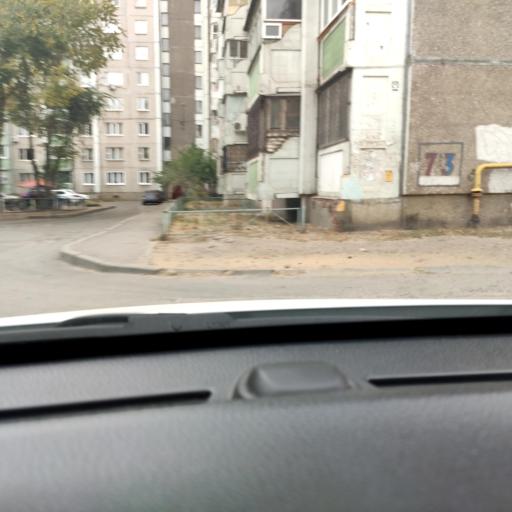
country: RU
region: Voronezj
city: Voronezh
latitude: 51.6543
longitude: 39.2418
